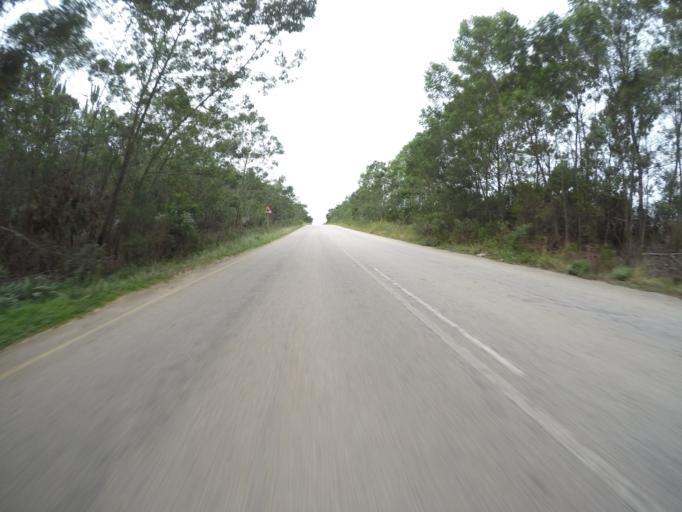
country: ZA
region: Eastern Cape
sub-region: Cacadu District Municipality
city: Kareedouw
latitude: -33.9969
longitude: 24.1613
